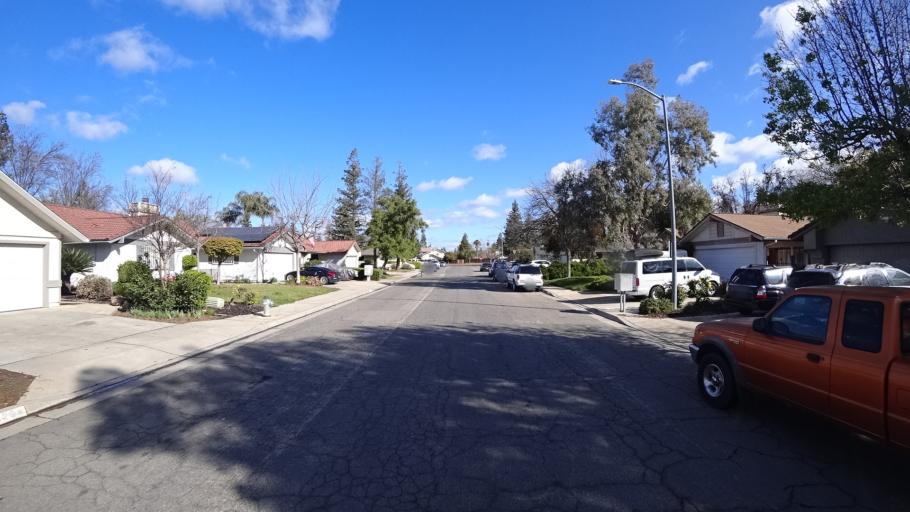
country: US
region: California
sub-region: Fresno County
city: West Park
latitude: 36.8251
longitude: -119.8812
